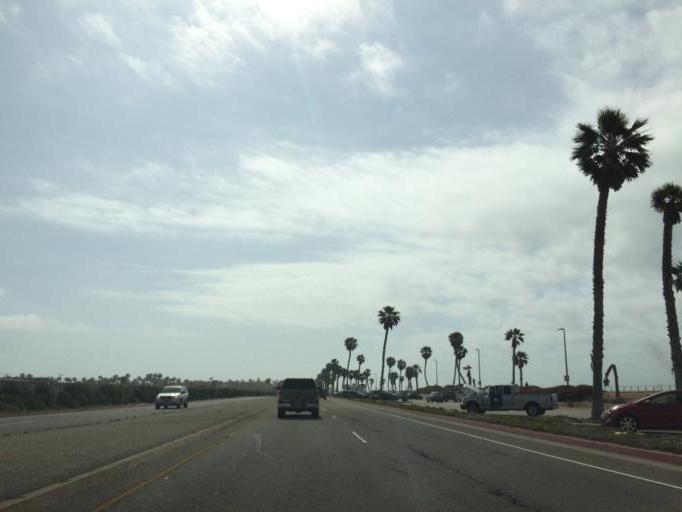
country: US
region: California
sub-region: Orange County
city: Huntington Beach
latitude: 33.6712
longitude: -118.0216
